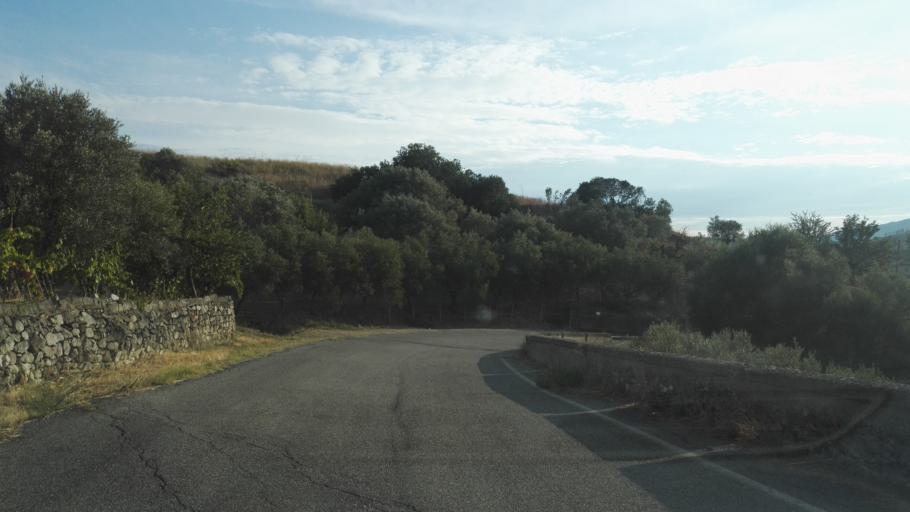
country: IT
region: Calabria
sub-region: Provincia di Reggio Calabria
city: Stignano
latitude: 38.3978
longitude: 16.4714
